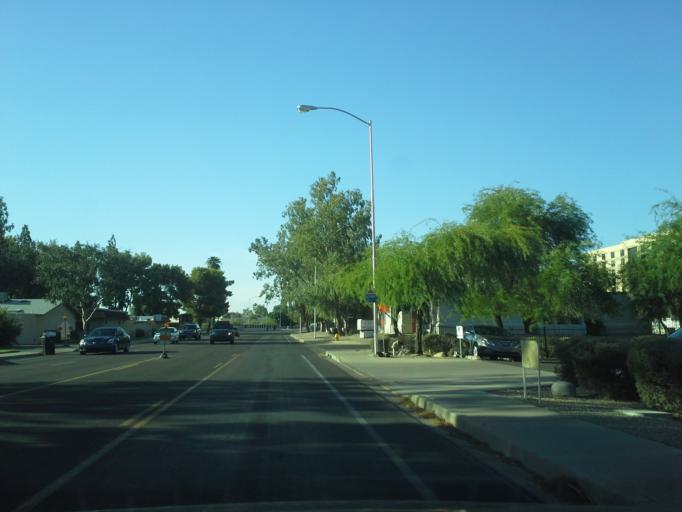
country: US
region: Arizona
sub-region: Maricopa County
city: Mesa
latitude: 33.4314
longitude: -111.8447
